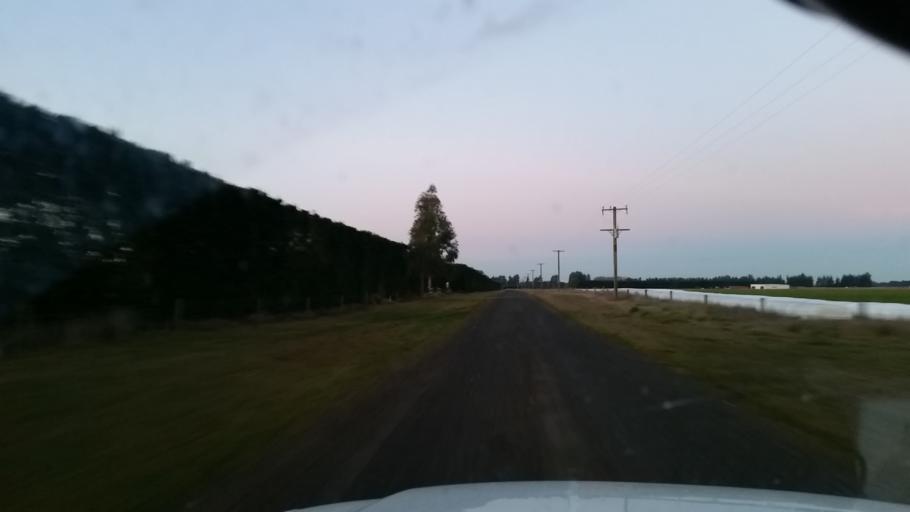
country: NZ
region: Canterbury
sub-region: Ashburton District
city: Tinwald
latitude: -43.9331
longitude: 171.5990
